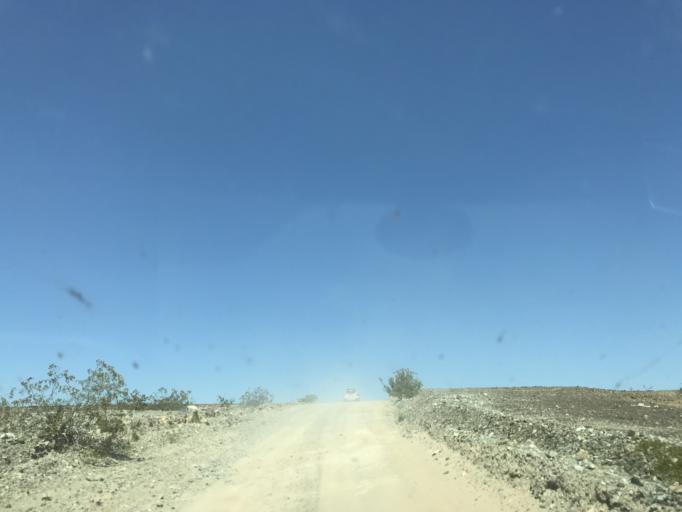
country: US
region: California
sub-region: Riverside County
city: Mesa Verde
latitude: 33.4991
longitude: -114.8494
